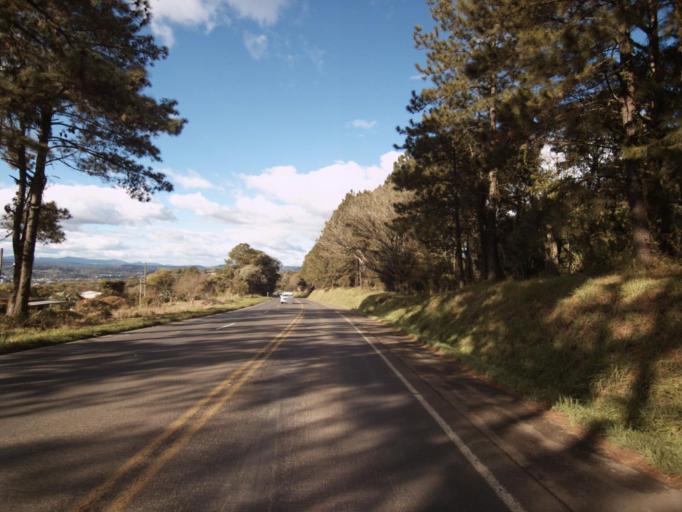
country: BR
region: Santa Catarina
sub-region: Joacaba
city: Joacaba
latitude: -27.1799
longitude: -51.5363
